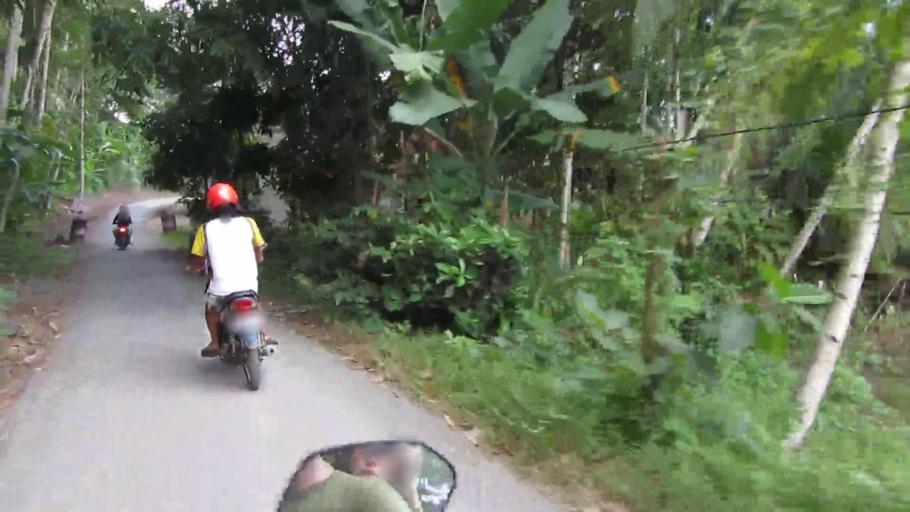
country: ID
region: West Java
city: Mandala
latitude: -7.7369
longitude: 108.4747
